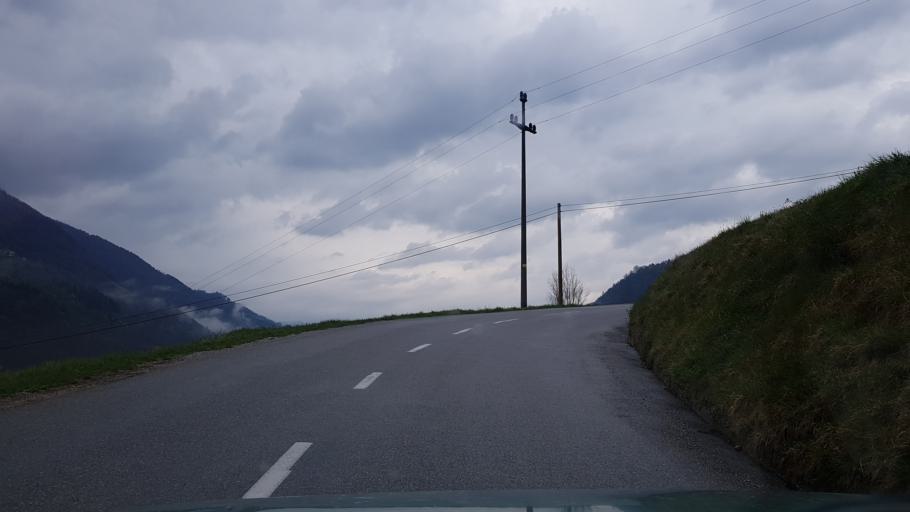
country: SI
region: Tolmin
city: Tolmin
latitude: 46.1187
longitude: 13.8117
